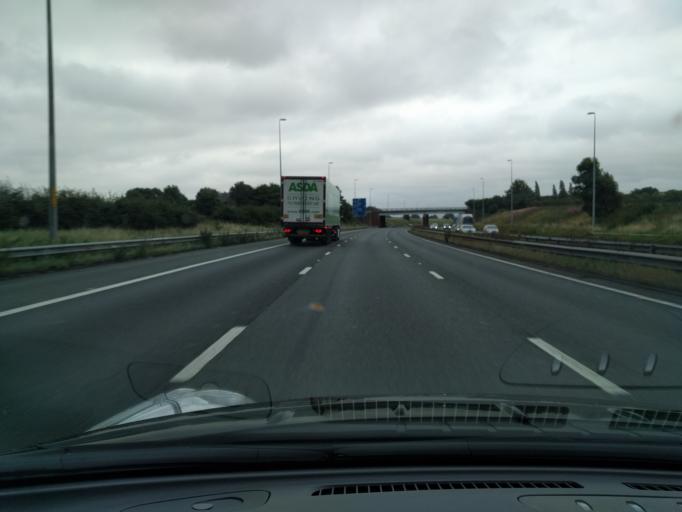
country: GB
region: England
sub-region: St. Helens
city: Newton-le-Willows
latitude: 53.4475
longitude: -2.5924
